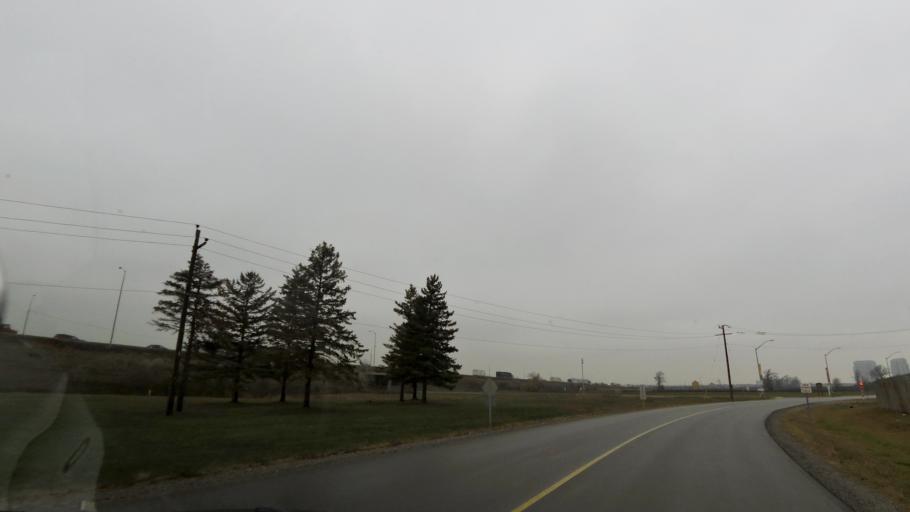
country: CA
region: Ontario
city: Etobicoke
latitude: 43.7068
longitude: -79.6117
